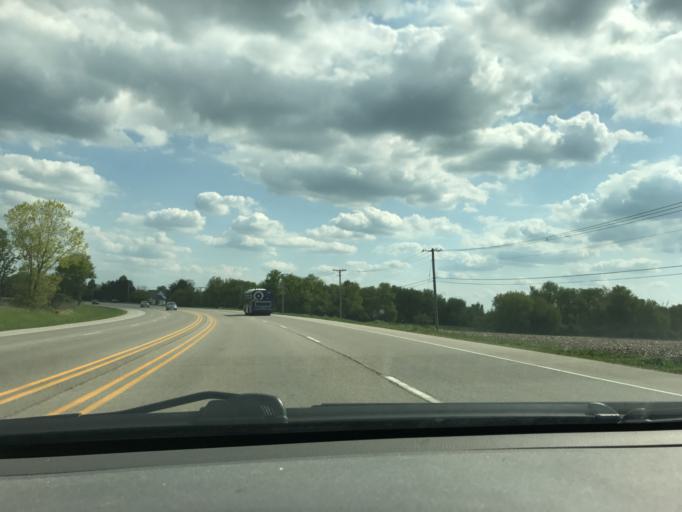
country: US
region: Illinois
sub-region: Kane County
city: South Elgin
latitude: 42.0231
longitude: -88.3395
